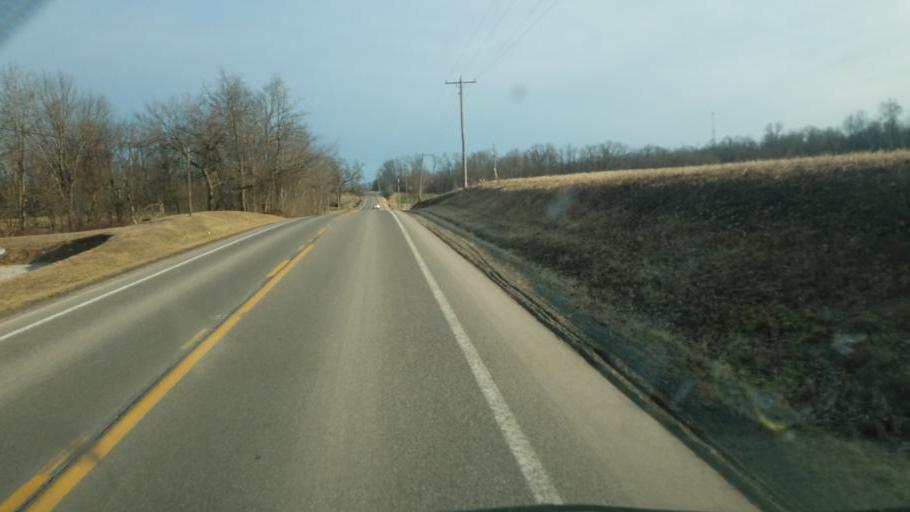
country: US
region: Ohio
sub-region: Knox County
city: Fredericktown
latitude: 40.5235
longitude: -82.6641
